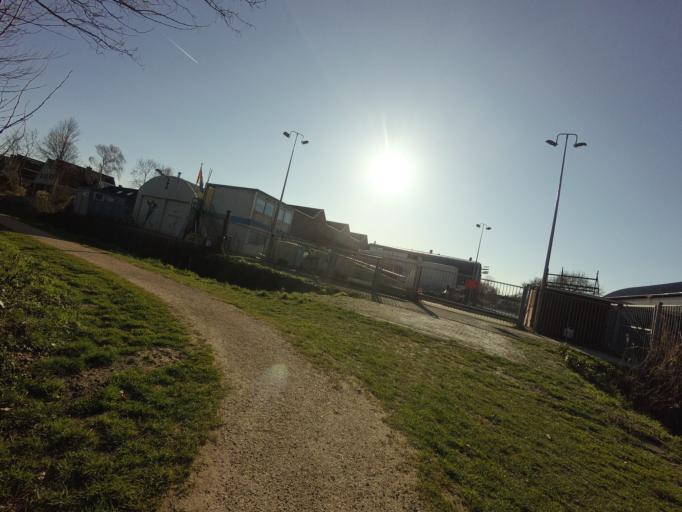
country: NL
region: Utrecht
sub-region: Stichtse Vecht
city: Vreeland
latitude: 52.2619
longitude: 5.0484
